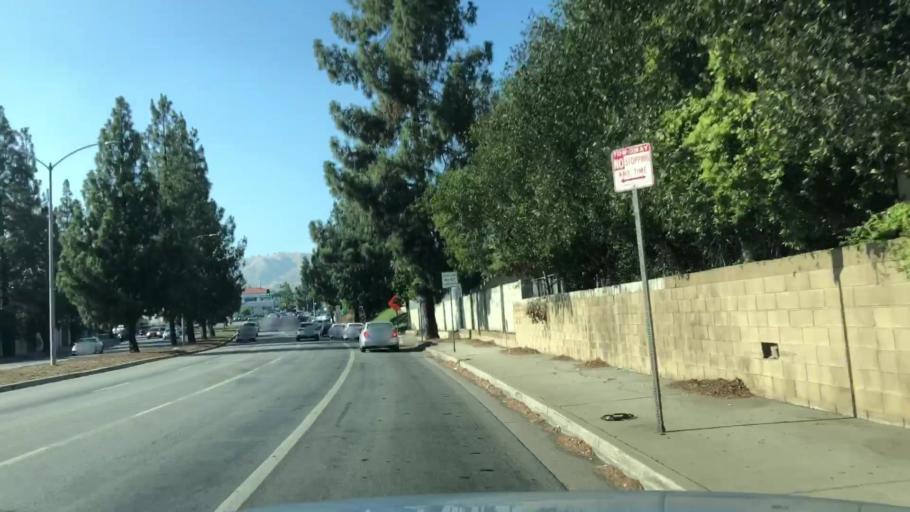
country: US
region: California
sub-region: Los Angeles County
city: Northridge
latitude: 34.2705
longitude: -118.5552
